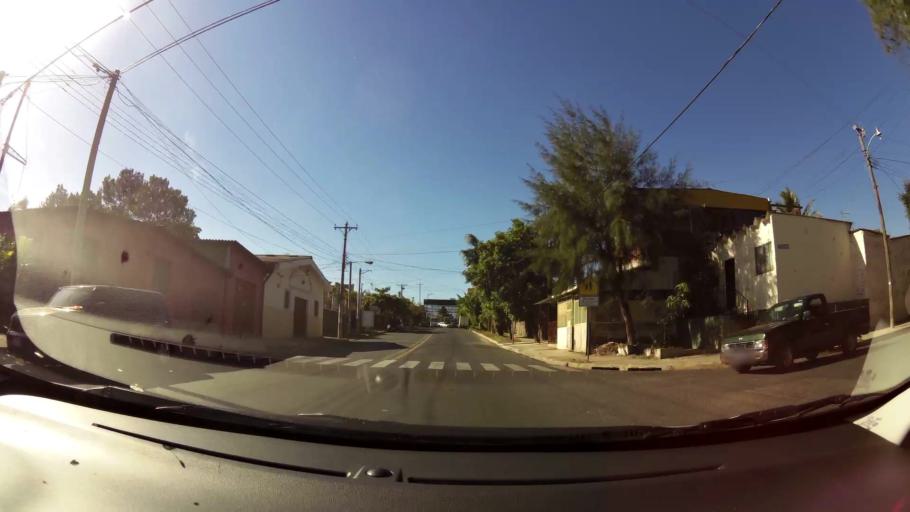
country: SV
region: Santa Ana
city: Santa Ana
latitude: 13.9711
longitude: -89.5726
